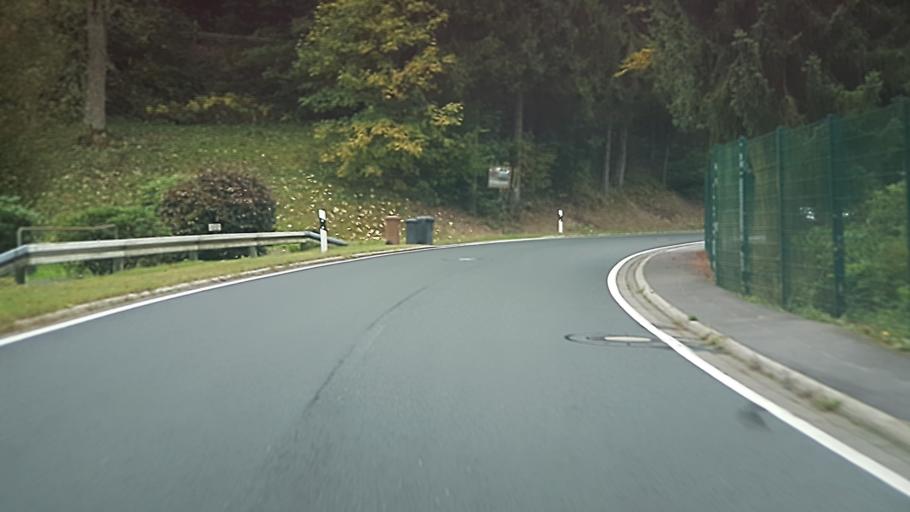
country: DE
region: North Rhine-Westphalia
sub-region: Regierungsbezirk Arnsberg
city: Herscheid
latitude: 51.1959
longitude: 7.6913
